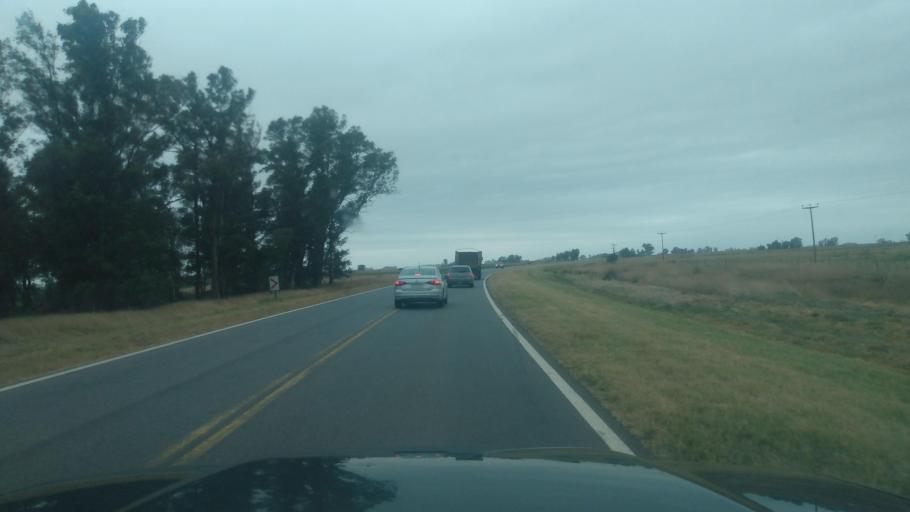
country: AR
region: Buenos Aires
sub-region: Partido de Nueve de Julio
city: Nueve de Julio
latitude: -35.4000
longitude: -60.7630
